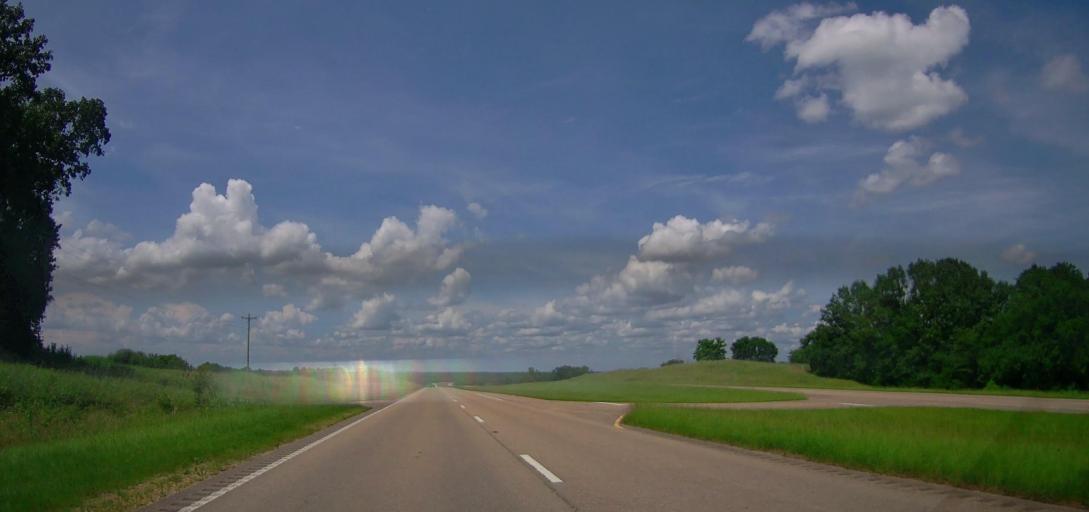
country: US
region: Mississippi
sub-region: Lee County
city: Nettleton
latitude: 34.0352
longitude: -88.6324
